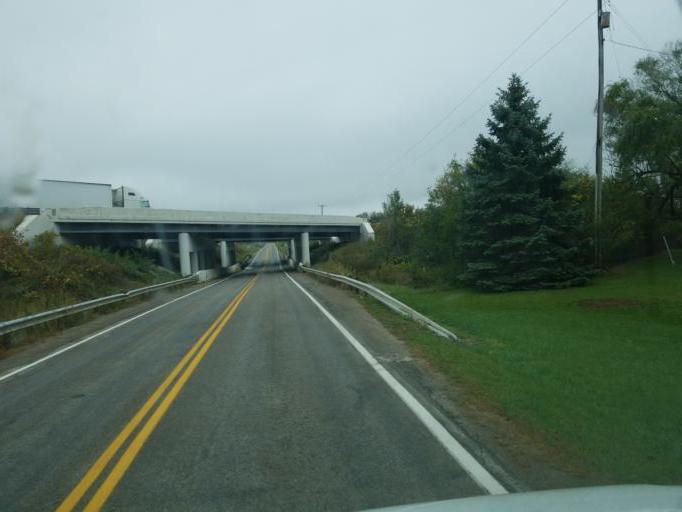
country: US
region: Ohio
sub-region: Ashland County
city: Ashland
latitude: 40.8221
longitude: -82.3355
